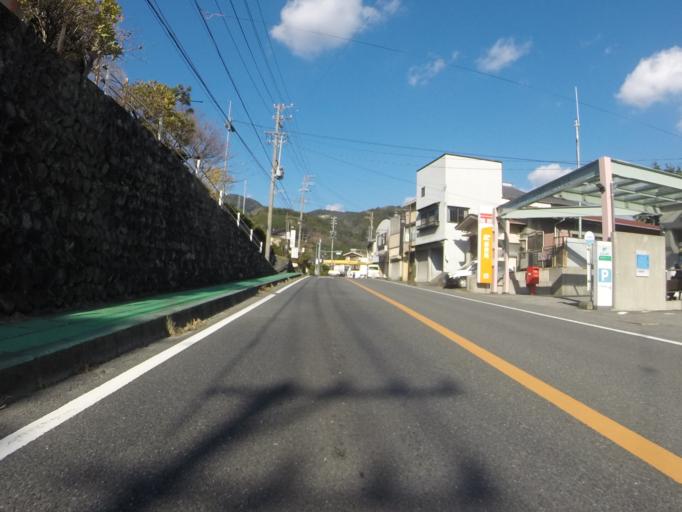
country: JP
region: Shizuoka
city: Fujinomiya
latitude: 35.0970
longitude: 138.5129
